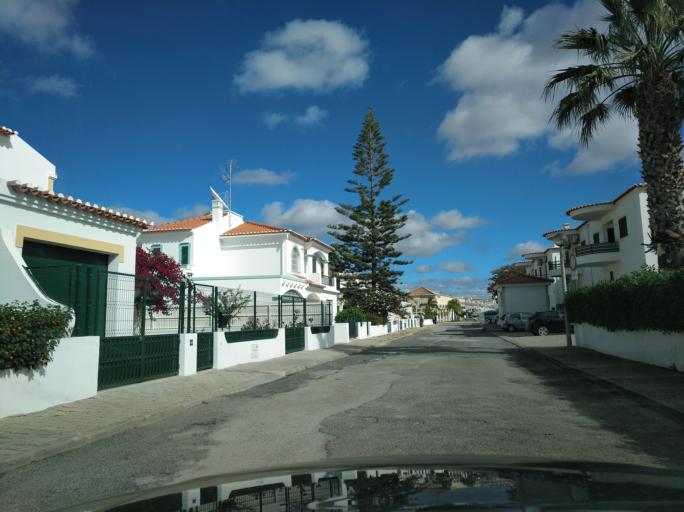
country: PT
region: Faro
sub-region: Vila Real de Santo Antonio
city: Monte Gordo
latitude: 37.1724
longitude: -7.5058
